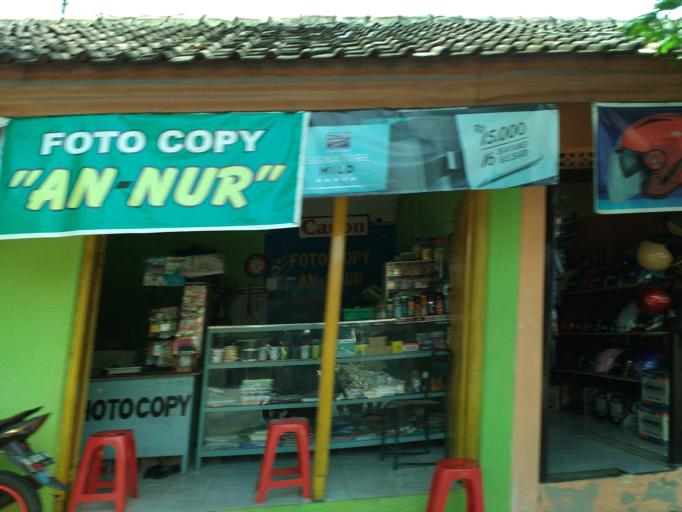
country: ID
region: Central Java
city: Klaten
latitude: -7.7068
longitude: 110.5973
